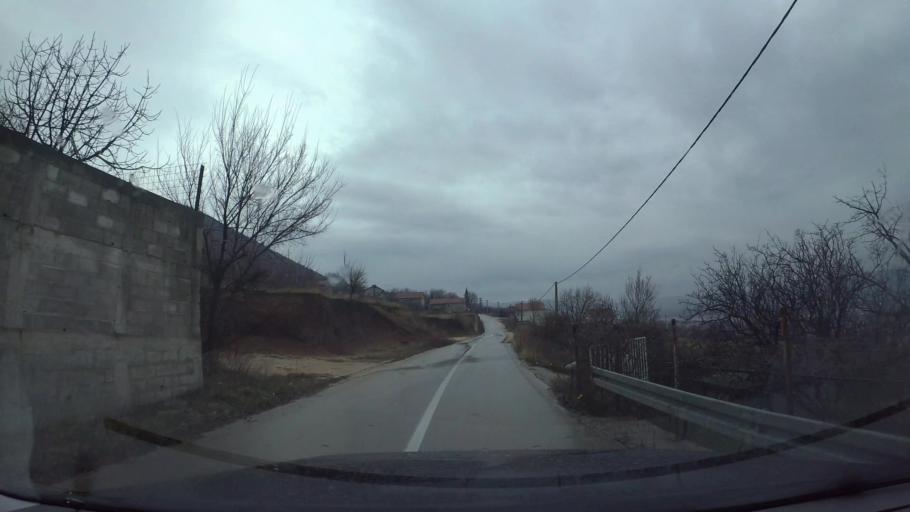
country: BA
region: Federation of Bosnia and Herzegovina
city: Rodoc
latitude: 43.3016
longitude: 17.8540
